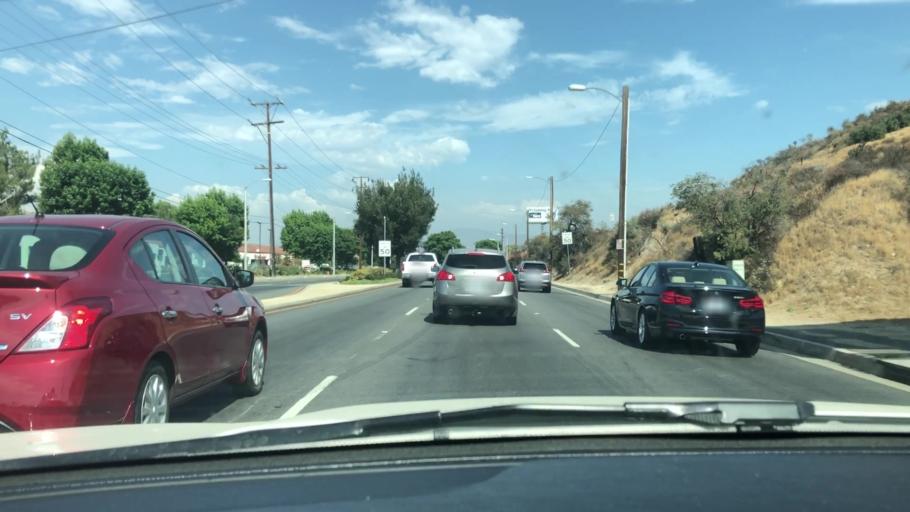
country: US
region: California
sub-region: Los Angeles County
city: Santa Clarita
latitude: 34.4223
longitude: -118.5391
